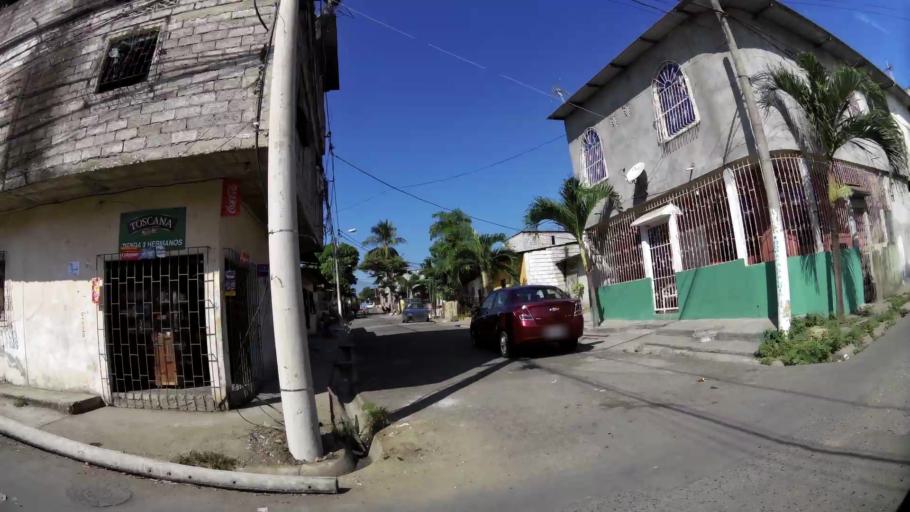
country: EC
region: Guayas
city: Eloy Alfaro
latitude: -2.0998
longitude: -79.9236
